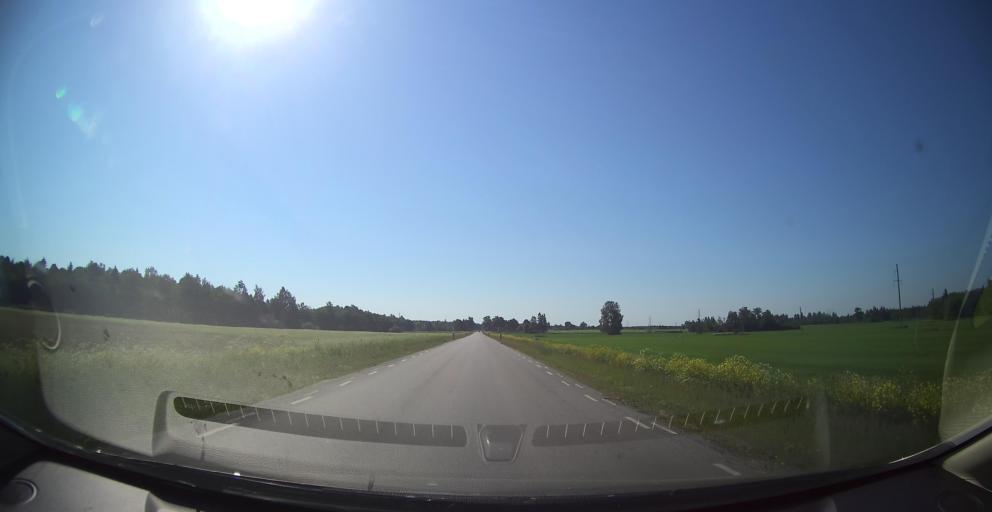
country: EE
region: Harju
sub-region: Raasiku vald
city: Raasiku
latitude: 59.3126
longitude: 25.1580
